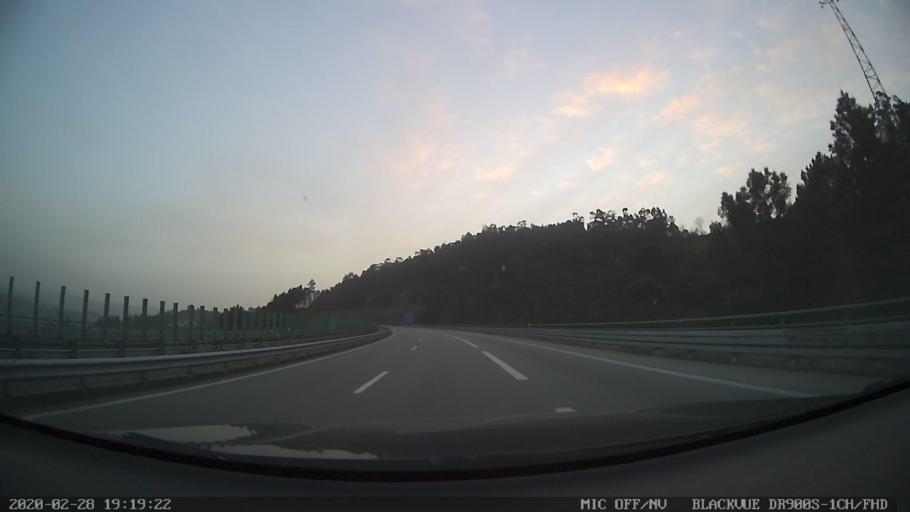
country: PT
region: Porto
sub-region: Marco de Canaveses
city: Marco de Canavezes
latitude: 41.2333
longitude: -8.1258
